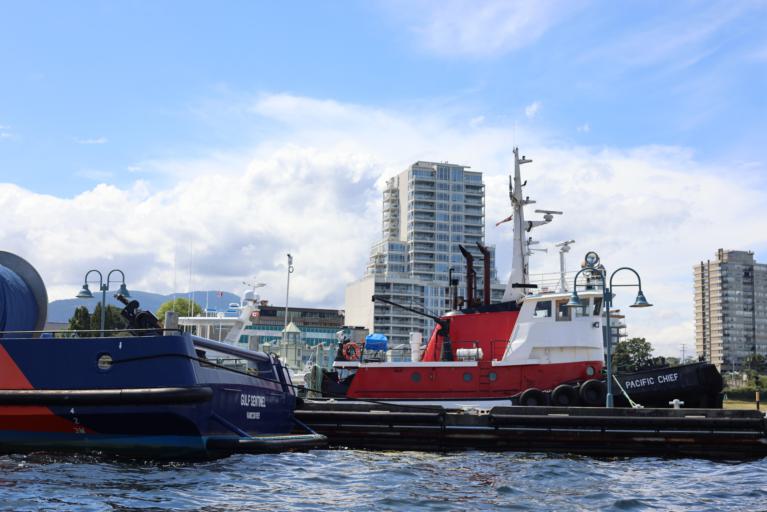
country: CA
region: British Columbia
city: Nanaimo
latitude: 49.1693
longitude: -123.9327
